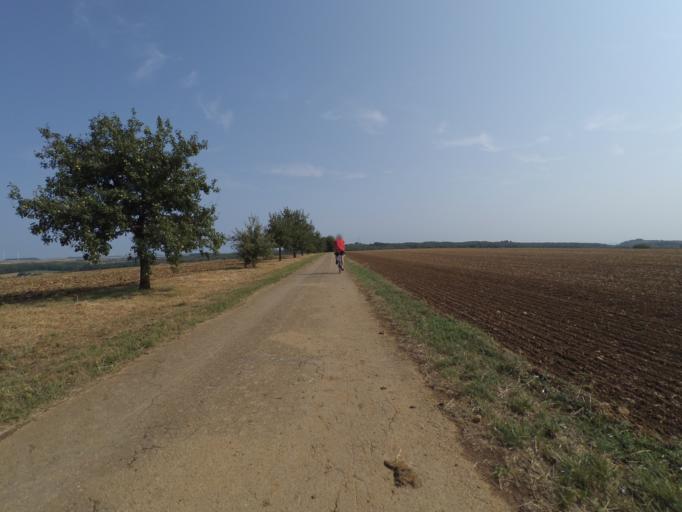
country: DE
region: Saarland
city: Perl
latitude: 49.4766
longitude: 6.4554
